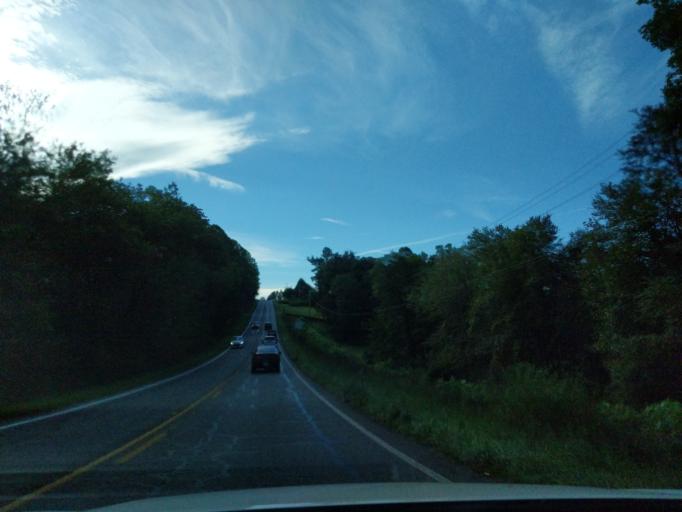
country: US
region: Georgia
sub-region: Fannin County
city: Blue Ridge
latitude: 34.8906
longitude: -84.3477
